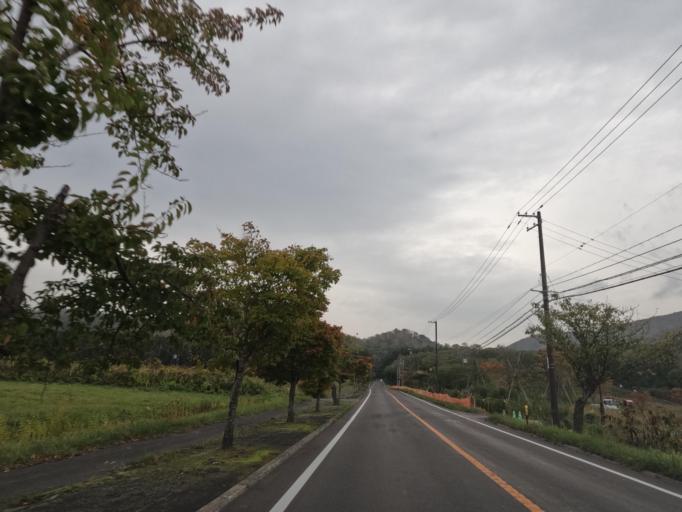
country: JP
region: Hokkaido
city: Date
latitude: 42.5545
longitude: 140.8626
